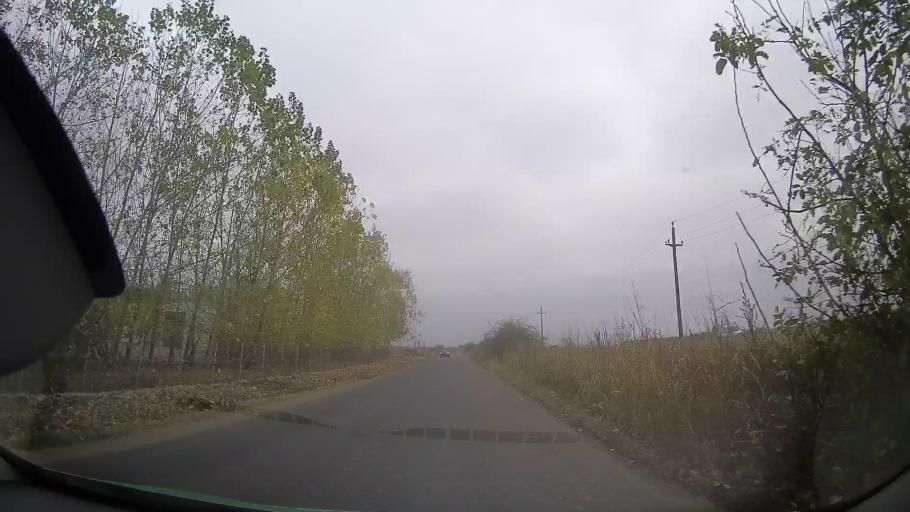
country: RO
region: Buzau
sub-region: Comuna Glodeanu-Silistea
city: Glodeanu-Silistea
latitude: 44.8172
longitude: 26.8420
